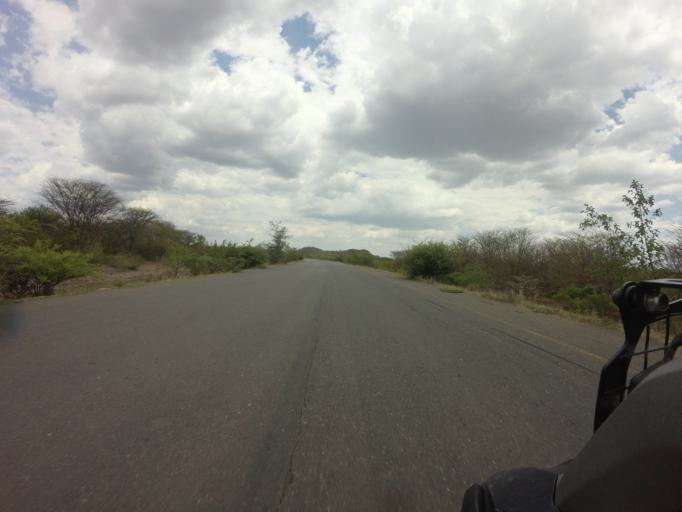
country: AO
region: Huila
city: Lubango
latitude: -15.3004
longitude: 13.8290
